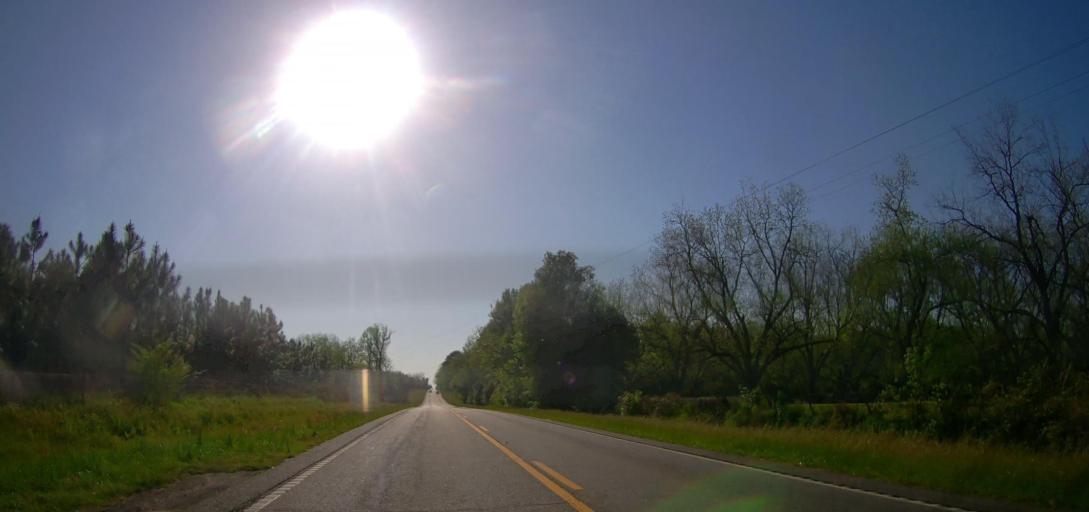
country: US
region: Georgia
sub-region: Ben Hill County
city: Fitzgerald
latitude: 31.7181
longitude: -83.3130
